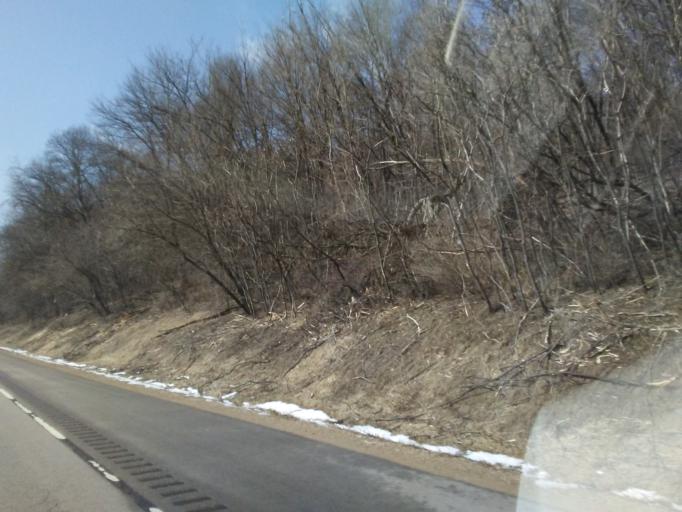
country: US
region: Wisconsin
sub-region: Richland County
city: Richland Center
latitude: 43.3485
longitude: -90.4533
